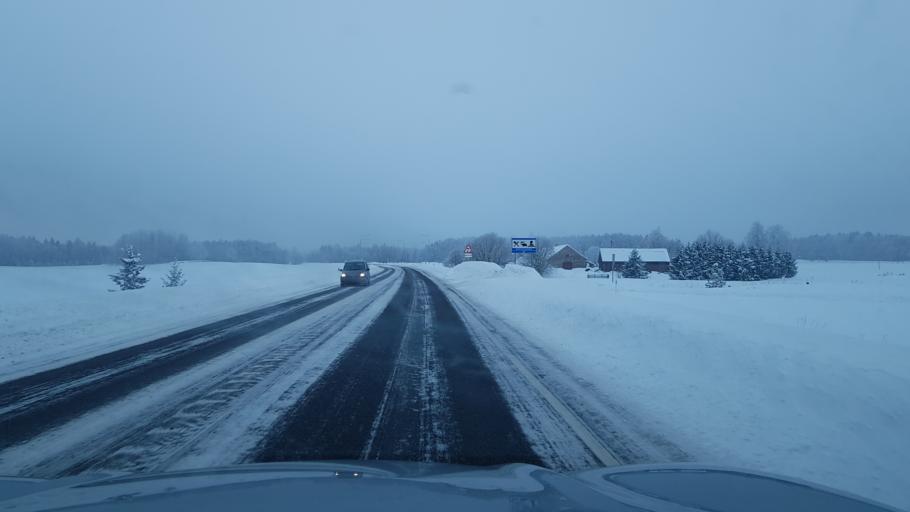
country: EE
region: Ida-Virumaa
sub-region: Johvi vald
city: Johvi
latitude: 59.2299
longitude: 27.3404
